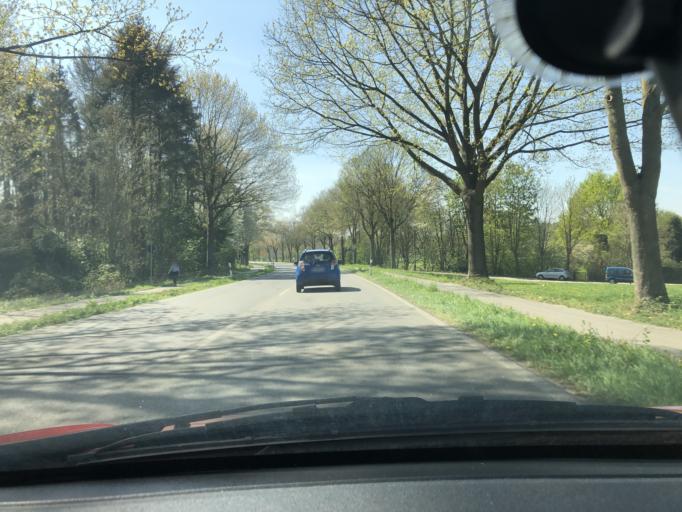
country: DE
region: North Rhine-Westphalia
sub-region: Regierungsbezirk Dusseldorf
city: Kamp-Lintfort
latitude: 51.5073
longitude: 6.5277
